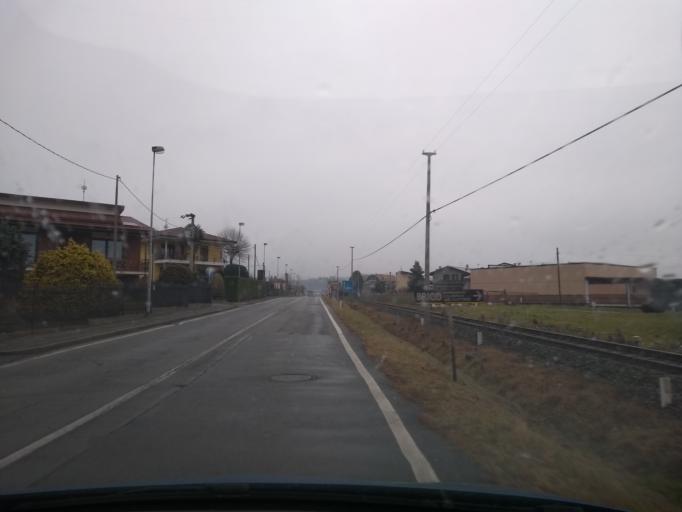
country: IT
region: Piedmont
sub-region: Provincia di Torino
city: Valperga
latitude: 45.3764
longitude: 7.6585
